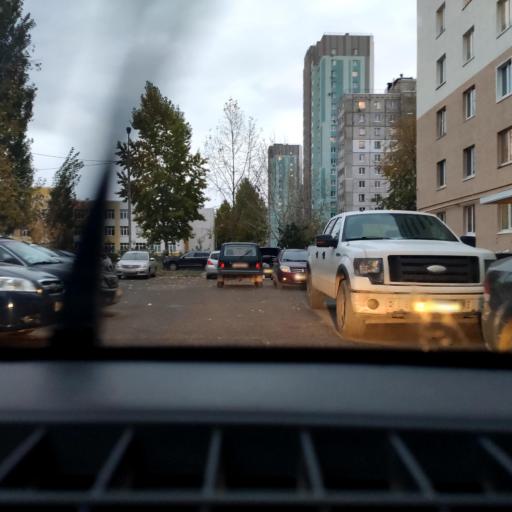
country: RU
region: Bashkortostan
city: Ufa
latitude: 54.7618
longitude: 56.0578
